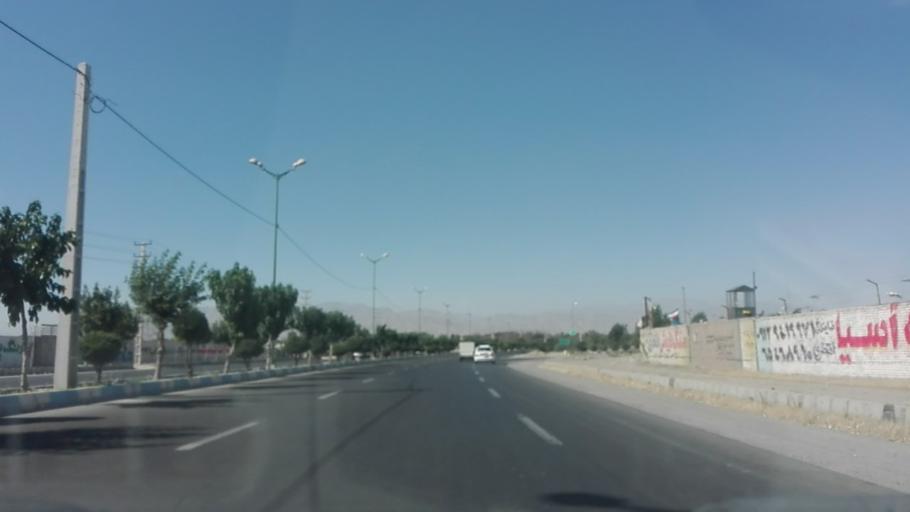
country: IR
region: Tehran
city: Shahriar
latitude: 35.6302
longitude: 51.0560
